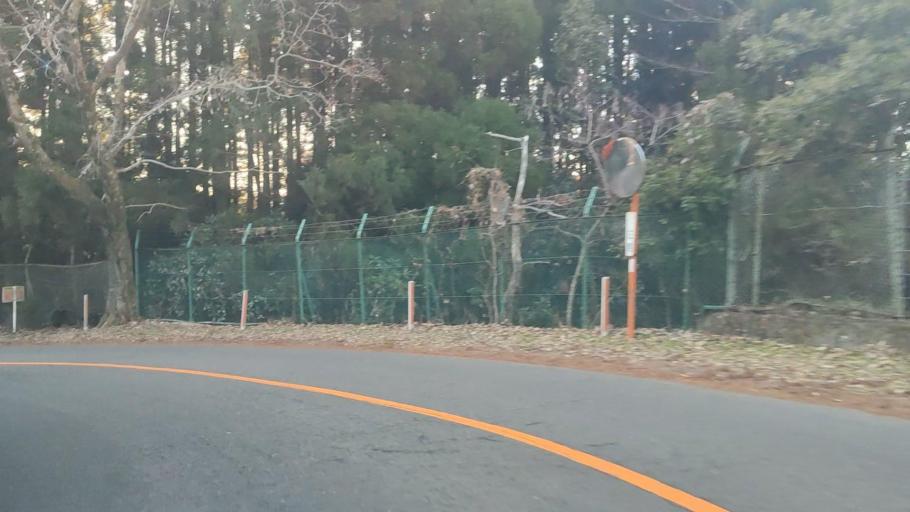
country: JP
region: Oita
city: Beppu
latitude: 33.2600
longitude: 131.3784
